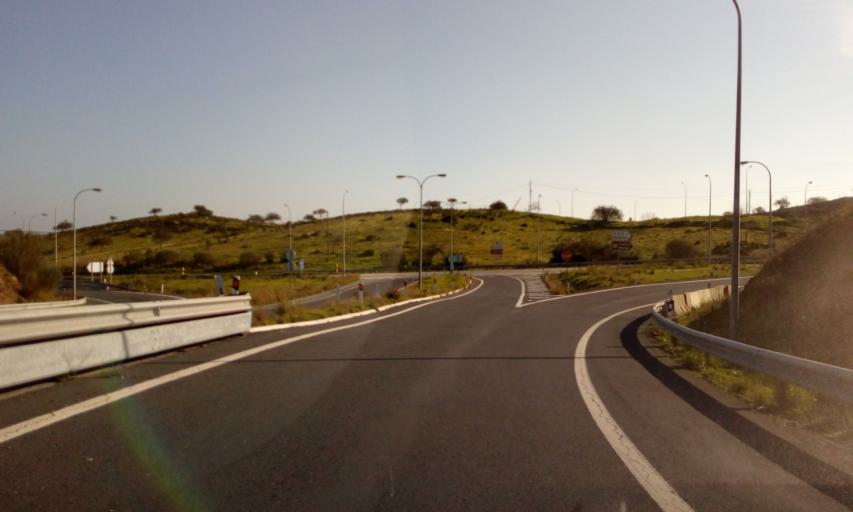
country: PT
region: Faro
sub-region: Castro Marim
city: Castro Marim
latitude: 37.2320
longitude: -7.4491
